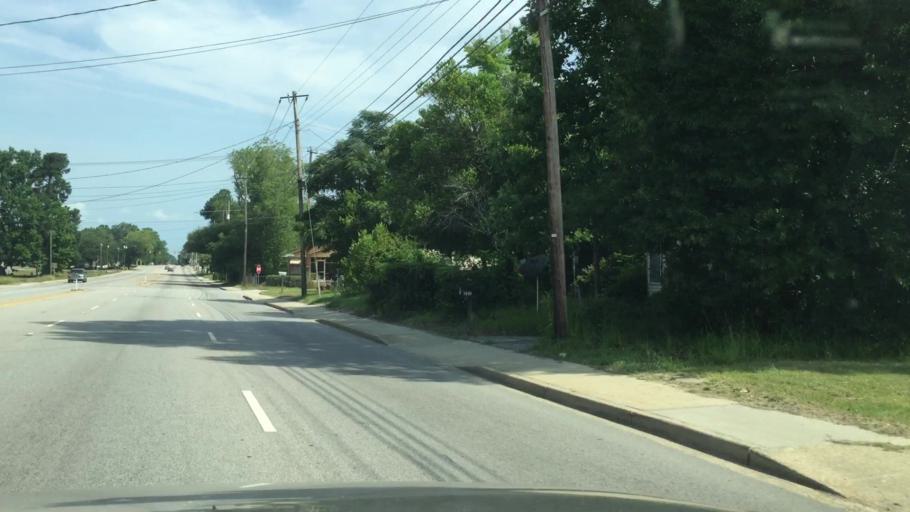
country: US
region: South Carolina
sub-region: Sumter County
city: South Sumter
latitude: 33.9166
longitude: -80.3572
